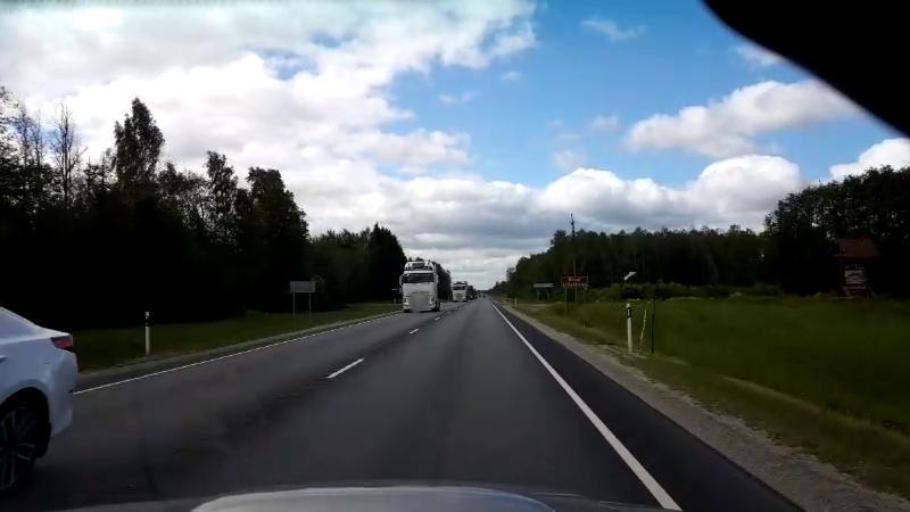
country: EE
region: Harju
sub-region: Nissi vald
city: Riisipere
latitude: 59.0706
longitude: 24.4519
